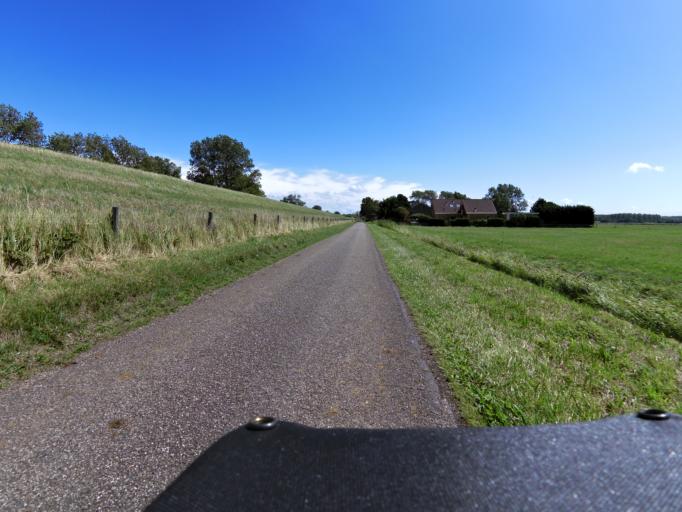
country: NL
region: South Holland
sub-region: Gemeente Goeree-Overflakkee
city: Goedereede
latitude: 51.8248
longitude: 4.0147
